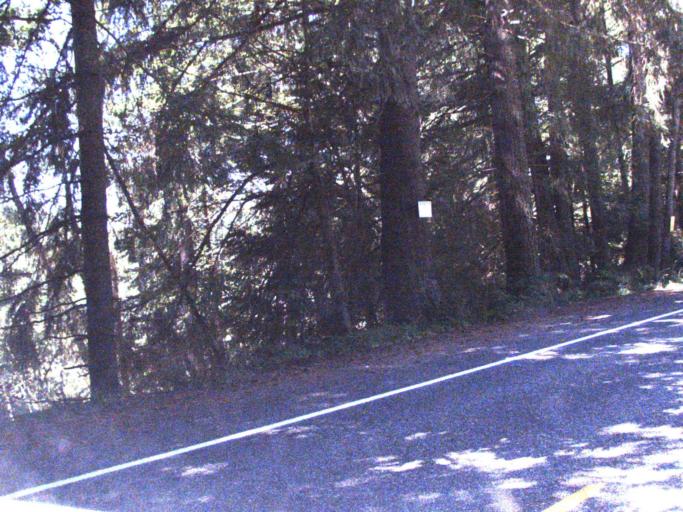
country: US
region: Washington
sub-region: King County
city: Enumclaw
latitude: 47.1732
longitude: -121.7751
